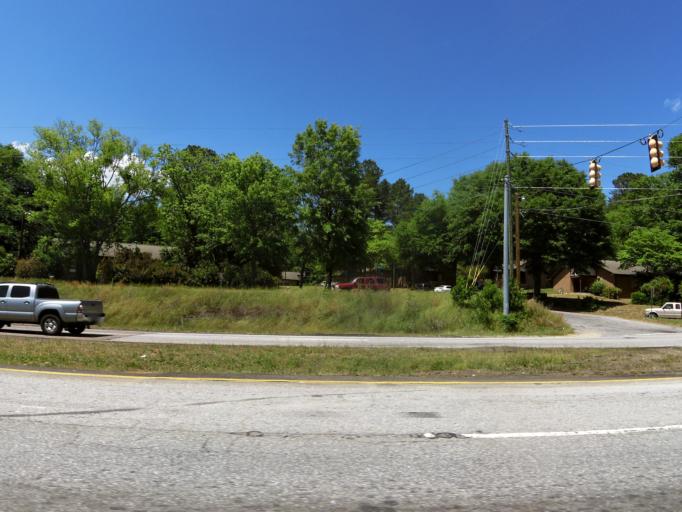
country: US
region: South Carolina
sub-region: Aiken County
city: Warrenville
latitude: 33.5563
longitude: -81.8021
